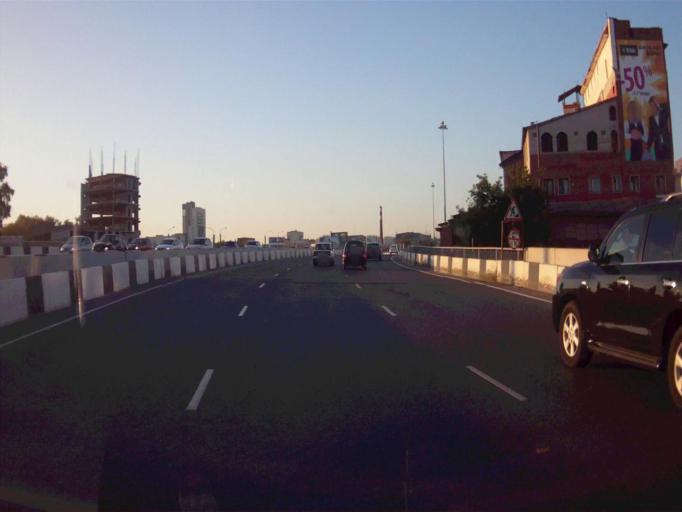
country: RU
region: Chelyabinsk
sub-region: Gorod Chelyabinsk
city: Chelyabinsk
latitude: 55.1692
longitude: 61.4125
